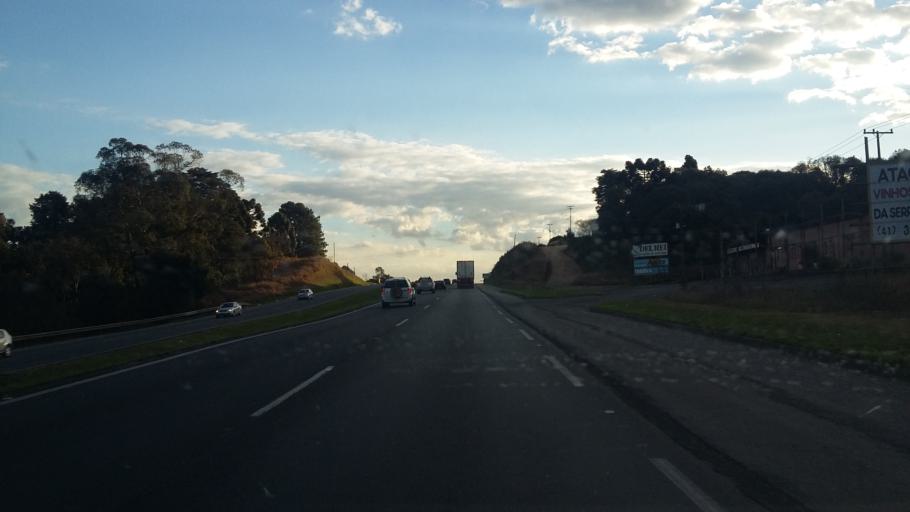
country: BR
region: Parana
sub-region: Campo Largo
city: Campo Largo
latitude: -25.4310
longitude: -49.4256
